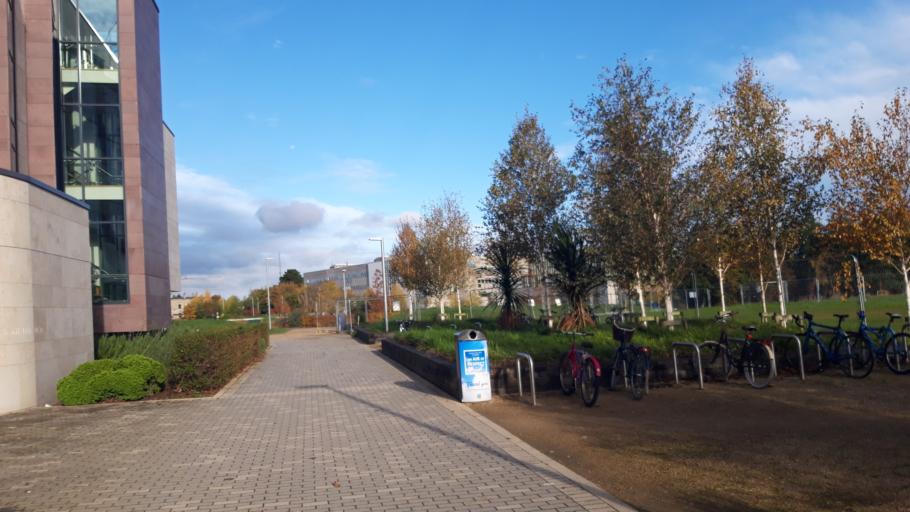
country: IE
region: Leinster
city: Mount Merrion
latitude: 53.3044
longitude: -6.2184
